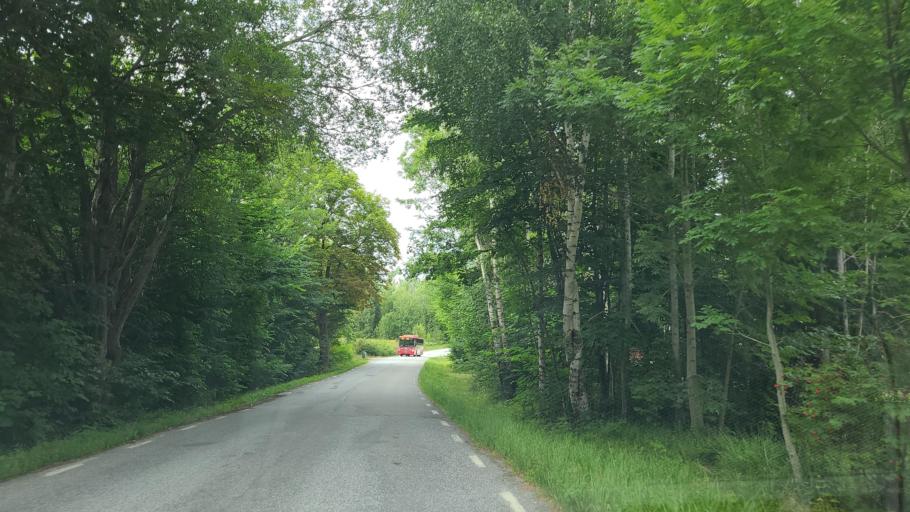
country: SE
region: Stockholm
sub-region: Upplands-Bro Kommun
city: Bro
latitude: 59.4894
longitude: 17.5672
